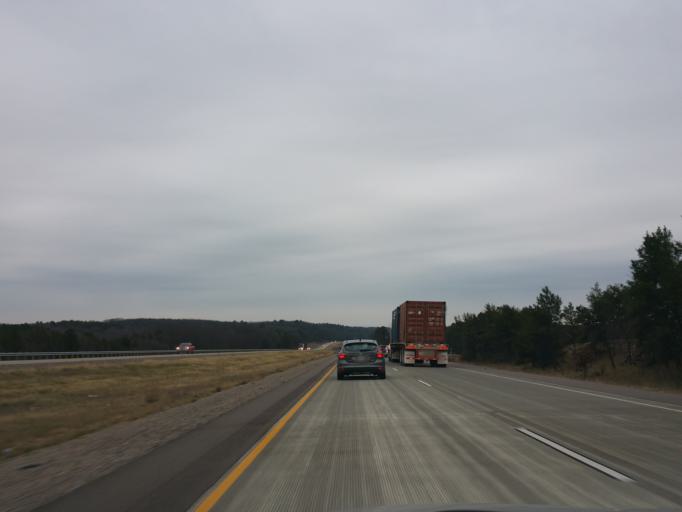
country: US
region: Wisconsin
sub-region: Jackson County
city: Black River Falls
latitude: 44.3376
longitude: -90.9078
